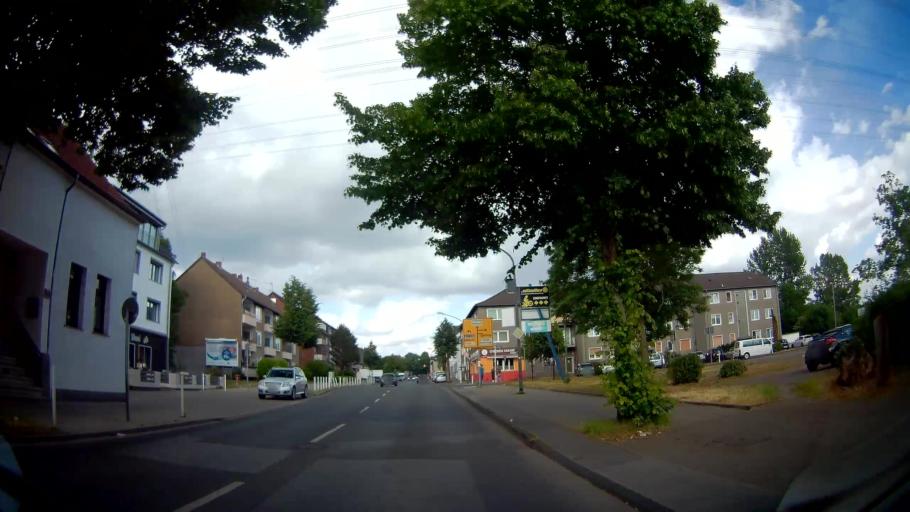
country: DE
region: North Rhine-Westphalia
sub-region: Regierungsbezirk Dusseldorf
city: Essen
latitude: 51.4918
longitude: 6.9941
